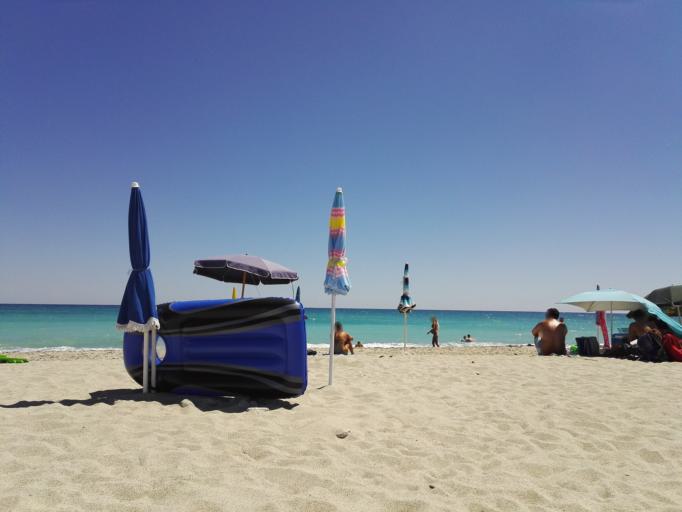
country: IT
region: Calabria
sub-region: Provincia di Catanzaro
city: Santa Caterina dello Ionio Marina
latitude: 38.5283
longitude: 16.5729
